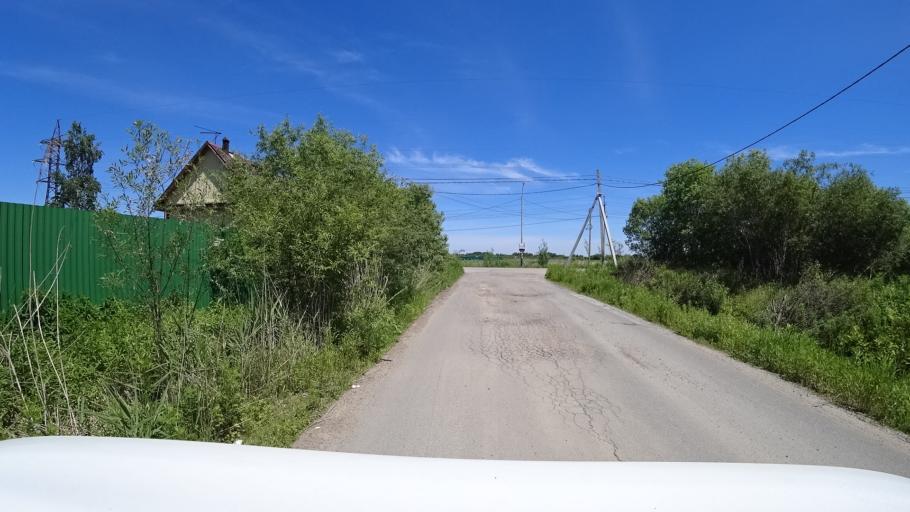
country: RU
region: Khabarovsk Krai
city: Topolevo
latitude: 48.4978
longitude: 135.1831
